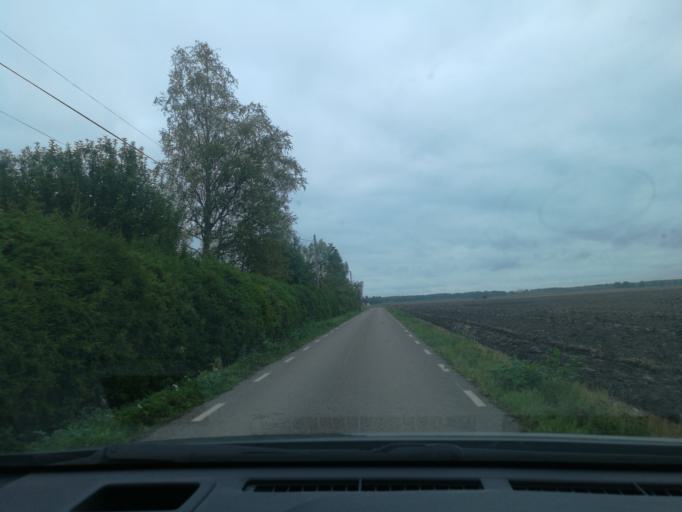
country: SE
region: Vaestmanland
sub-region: Vasteras
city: Tillberga
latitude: 59.7744
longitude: 16.6468
